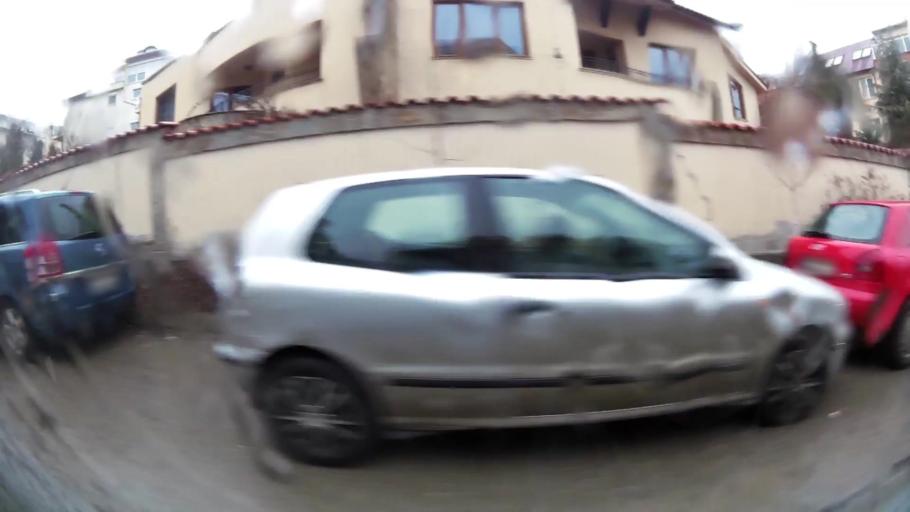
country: BG
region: Sofia-Capital
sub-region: Stolichna Obshtina
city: Sofia
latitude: 42.6437
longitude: 23.3317
